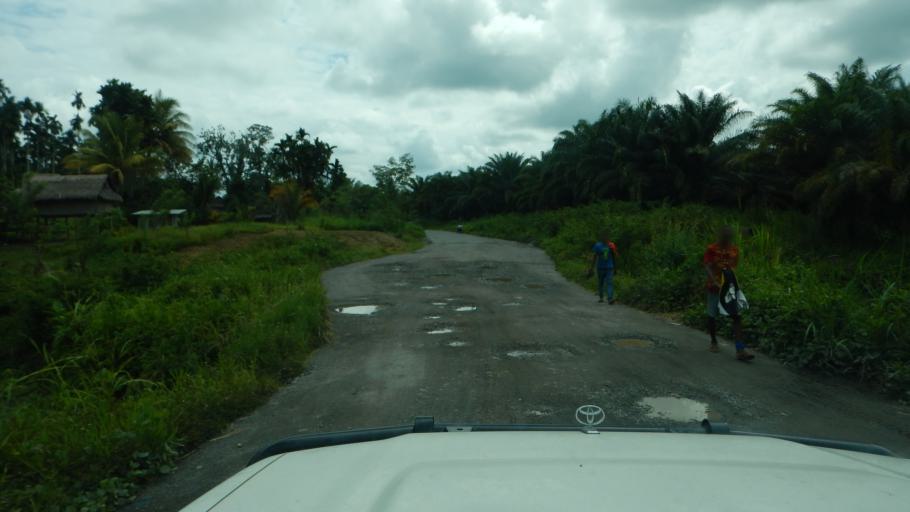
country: PG
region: Northern Province
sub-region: Sohe
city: Popondetta
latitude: -8.8240
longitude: 148.0864
